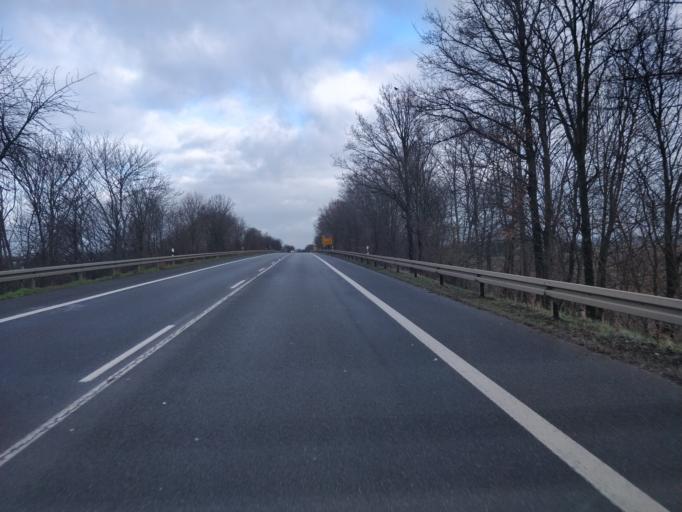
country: DE
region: North Rhine-Westphalia
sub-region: Regierungsbezirk Koln
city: Euskirchen
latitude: 50.6549
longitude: 6.8434
